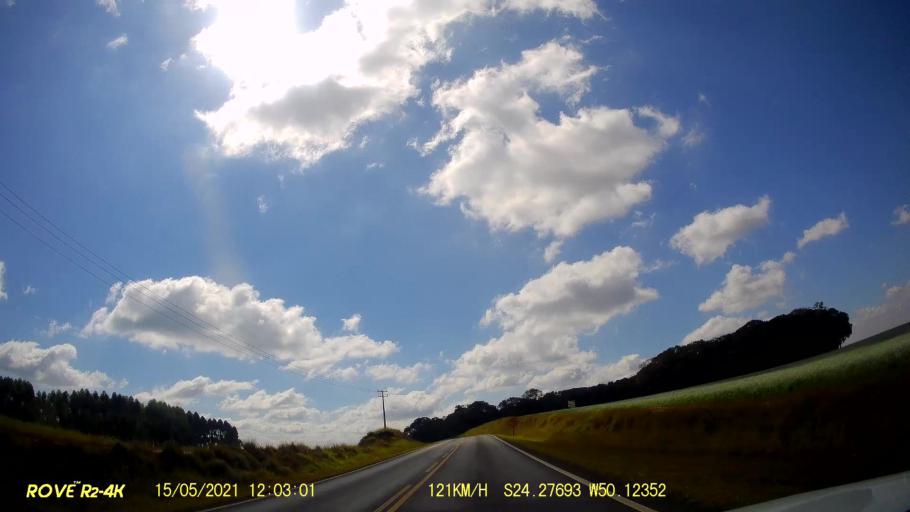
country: BR
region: Parana
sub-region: Pirai Do Sul
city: Pirai do Sul
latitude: -24.2771
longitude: -50.1236
